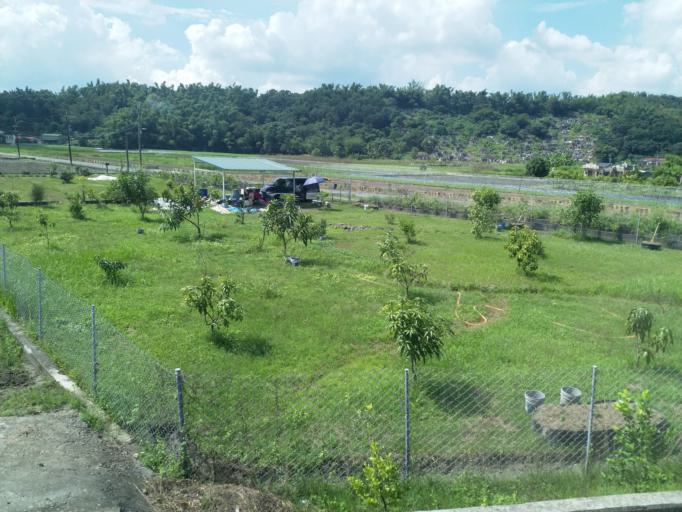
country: TW
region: Taiwan
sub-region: Pingtung
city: Pingtung
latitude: 22.8967
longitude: 120.5795
